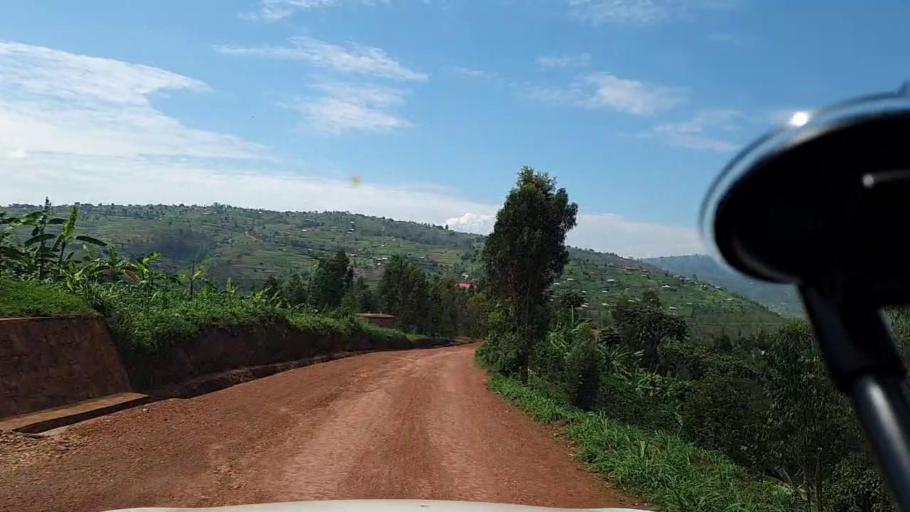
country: RW
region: Kigali
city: Kigali
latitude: -1.7983
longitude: 29.8971
